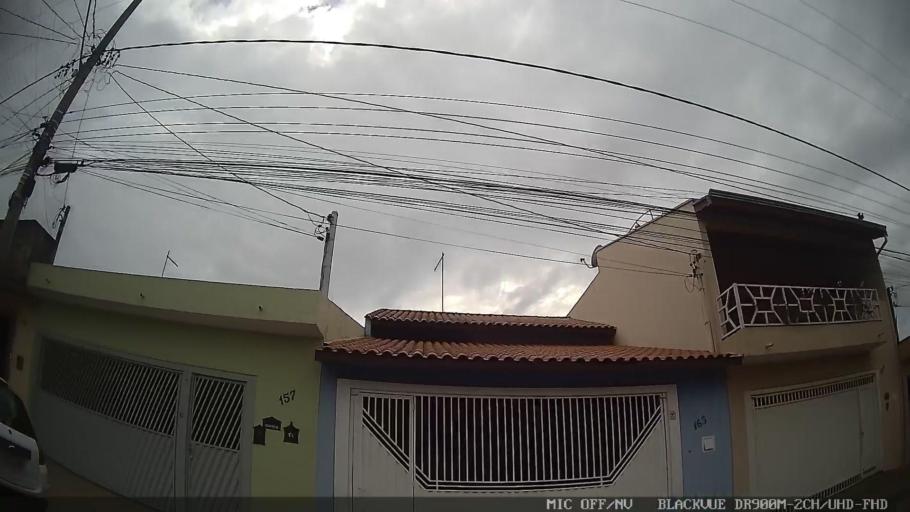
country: BR
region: Sao Paulo
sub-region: Salto
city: Salto
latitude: -23.2153
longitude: -47.2841
